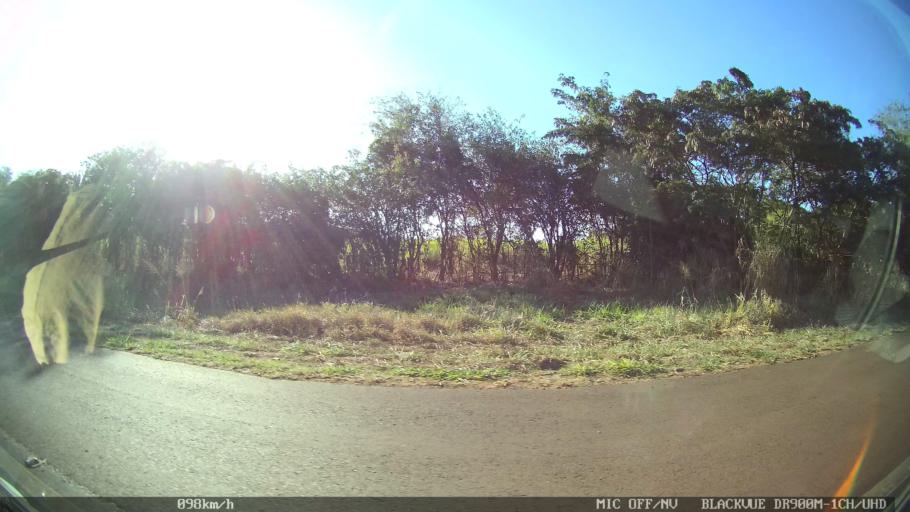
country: BR
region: Sao Paulo
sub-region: Guapiacu
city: Guapiacu
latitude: -20.7551
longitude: -49.1539
